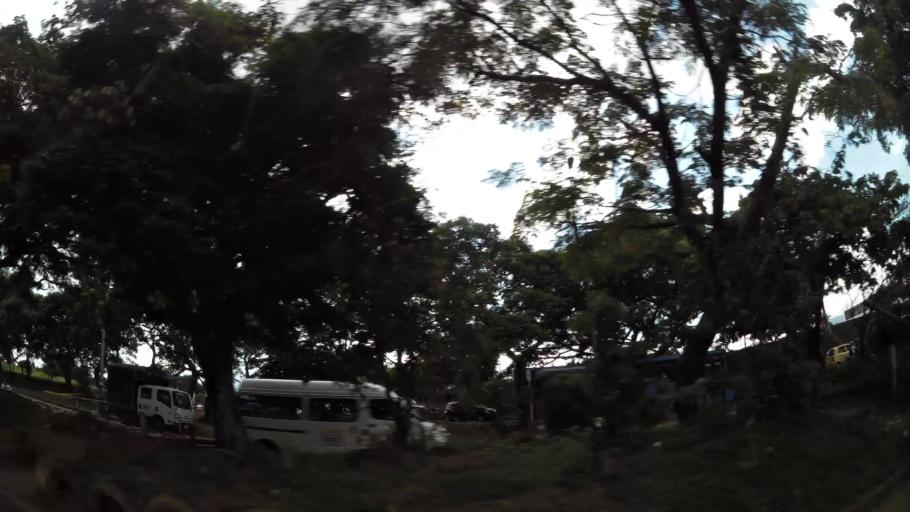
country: CO
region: Valle del Cauca
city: Cali
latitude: 3.4118
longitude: -76.5213
